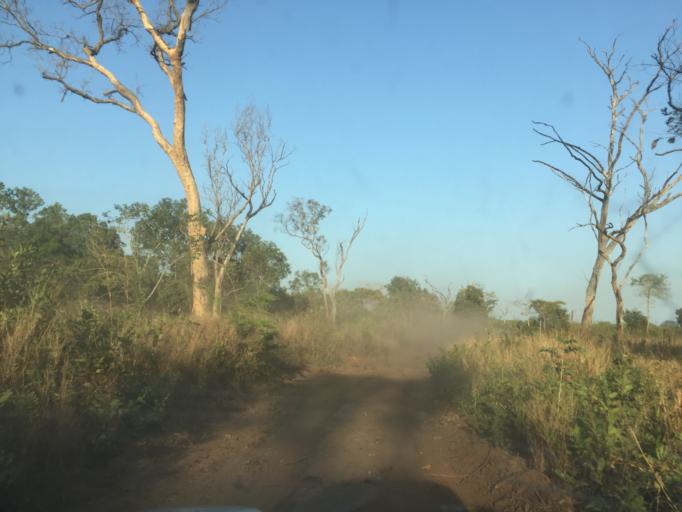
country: GW
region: Oio
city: Farim
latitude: 12.5287
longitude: -15.2780
